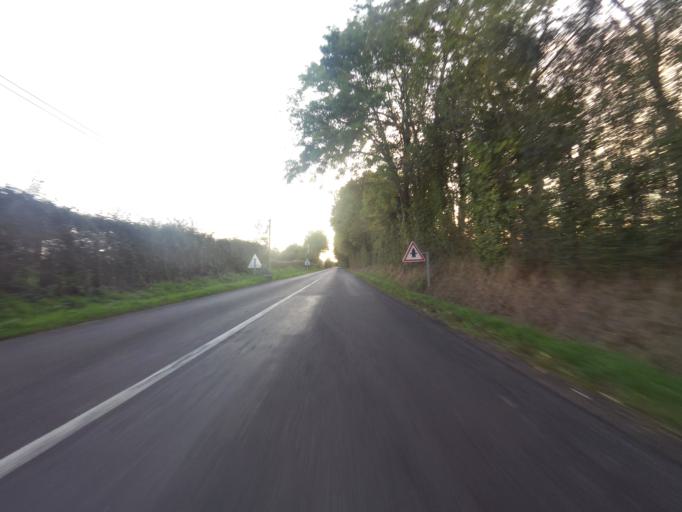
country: FR
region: Lower Normandy
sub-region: Departement du Calvados
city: La Vespiere
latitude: 49.0080
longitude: 0.3969
